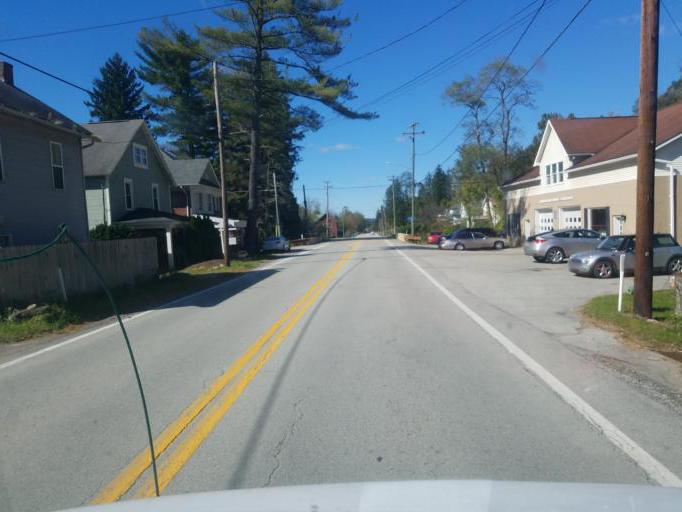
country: US
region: Pennsylvania
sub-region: Westmoreland County
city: Ligonier
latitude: 40.2129
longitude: -79.2006
